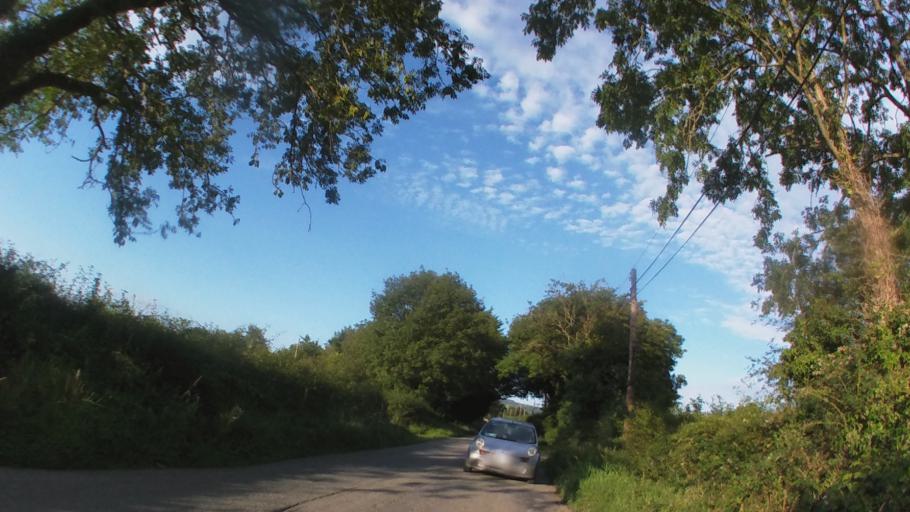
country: IE
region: Leinster
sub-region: Kilkenny
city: Kilkenny
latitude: 52.6766
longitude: -7.1882
